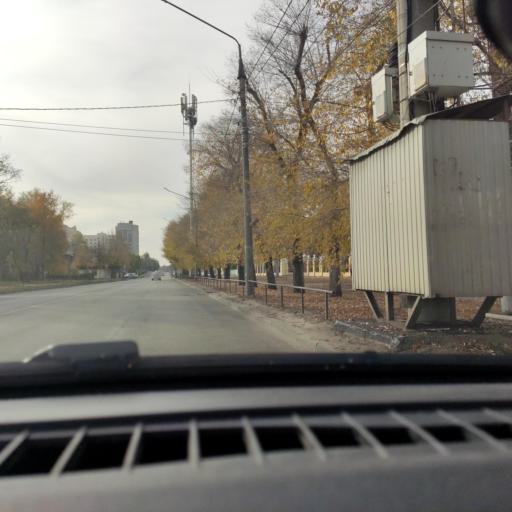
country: RU
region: Voronezj
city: Voronezh
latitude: 51.6416
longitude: 39.1774
